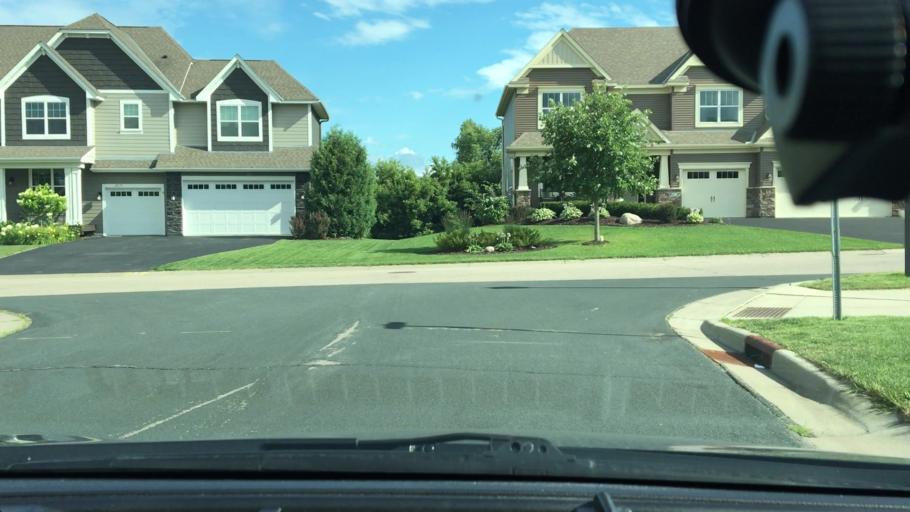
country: US
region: Minnesota
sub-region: Carver County
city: Victoria
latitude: 44.8547
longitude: -93.6853
